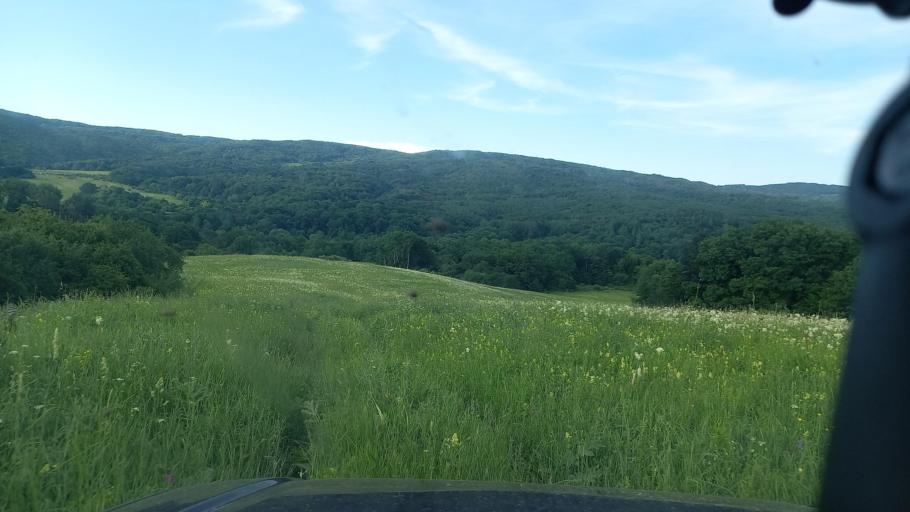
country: RU
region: Karachayevo-Cherkesiya
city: Kurdzhinovo
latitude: 44.1304
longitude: 41.0945
